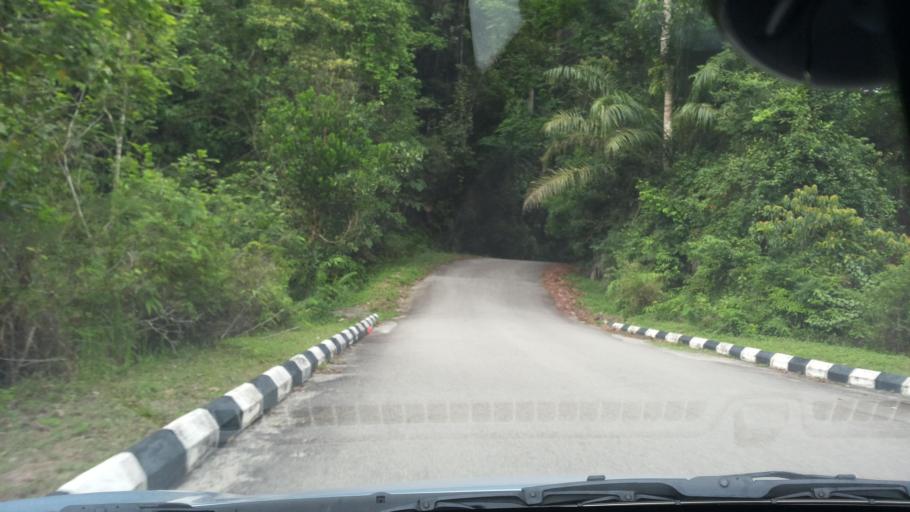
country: MY
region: Pahang
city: Kuantan
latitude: 3.7915
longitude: 103.1487
